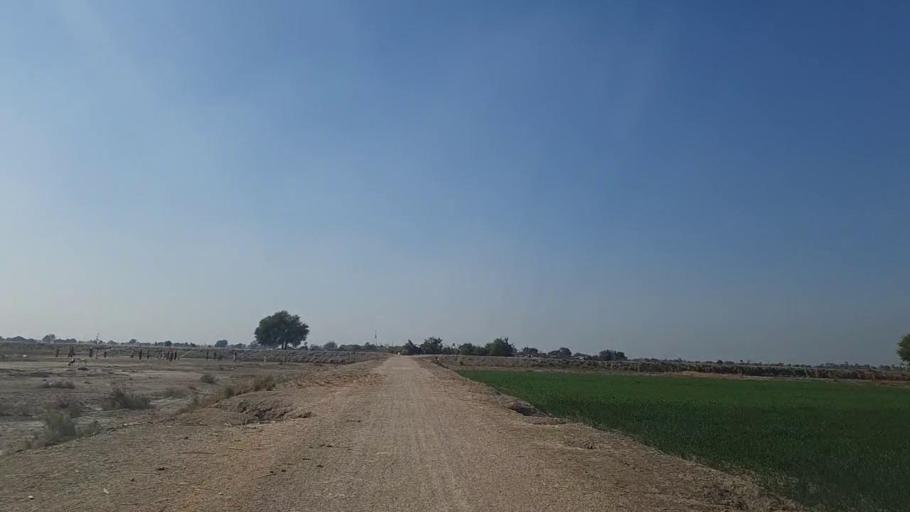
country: PK
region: Sindh
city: Jam Sahib
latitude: 26.2177
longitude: 68.5859
